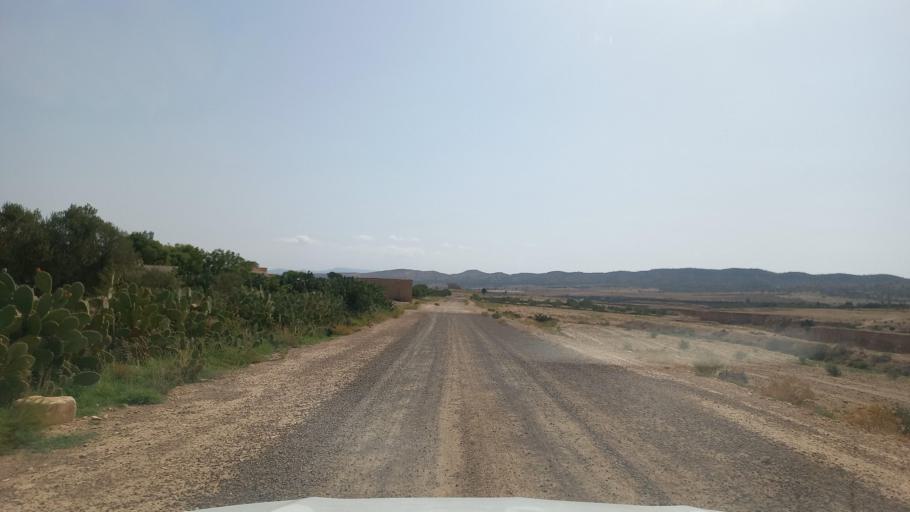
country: TN
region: Al Qasrayn
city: Sbiba
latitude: 35.3936
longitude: 8.9541
